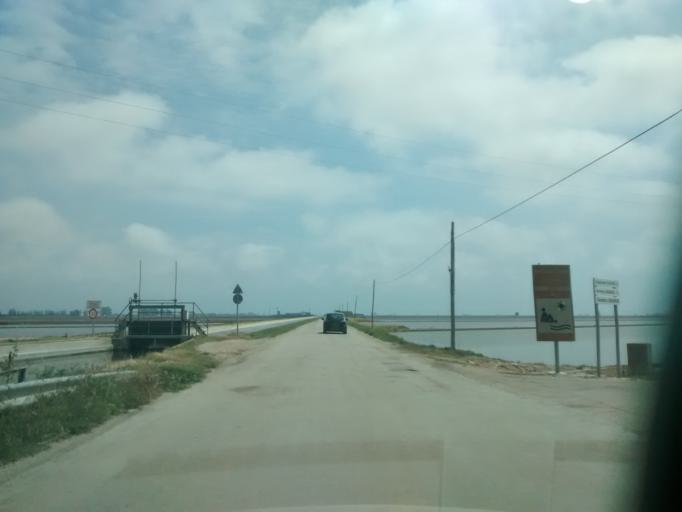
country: ES
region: Catalonia
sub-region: Provincia de Tarragona
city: Deltebre
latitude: 40.7020
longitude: 0.7410
